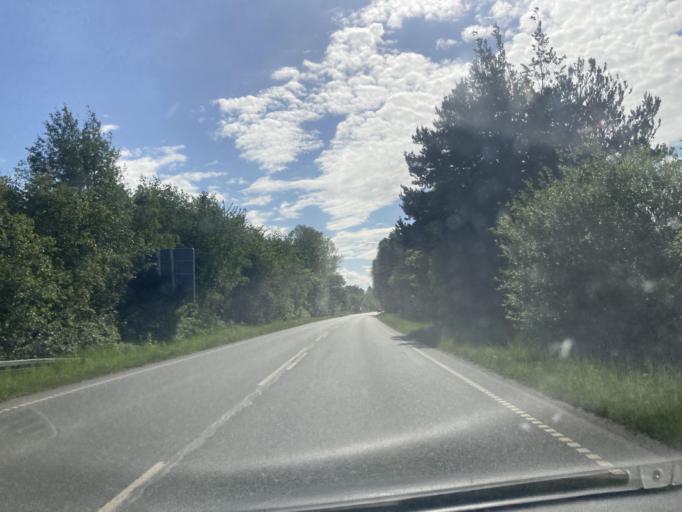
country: DK
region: Capital Region
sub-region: Gribskov Kommune
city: Helsinge
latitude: 56.0230
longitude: 12.1703
